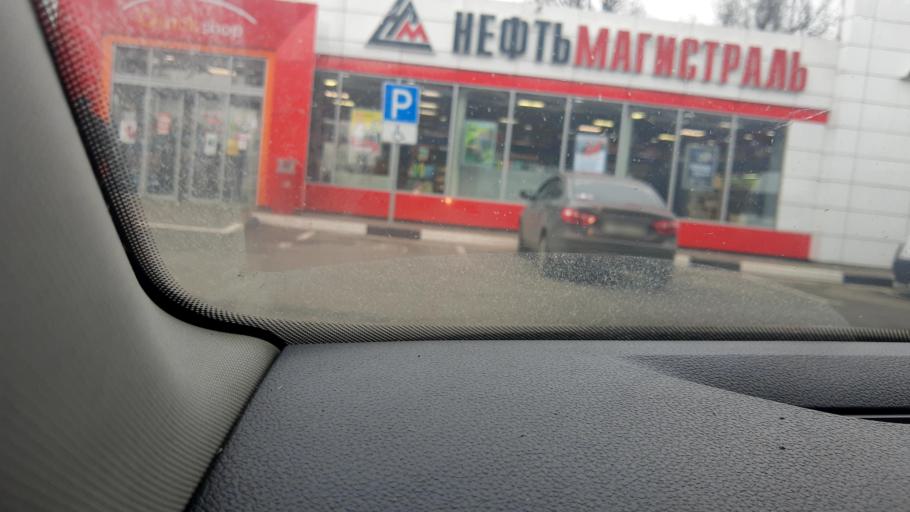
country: RU
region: Moskovskaya
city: Shcherbinka
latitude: 55.4922
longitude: 37.6126
